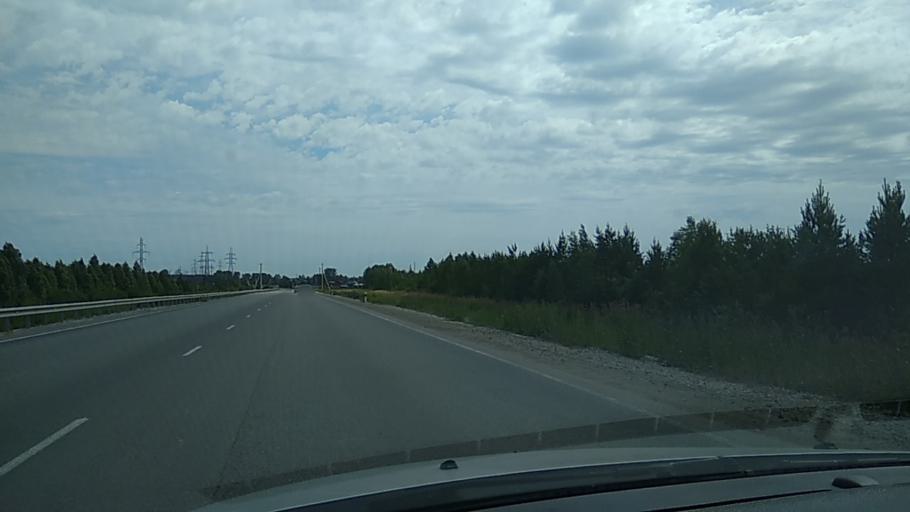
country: RU
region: Sverdlovsk
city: Verkhnyaya Pyshma
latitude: 56.9508
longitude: 60.5901
